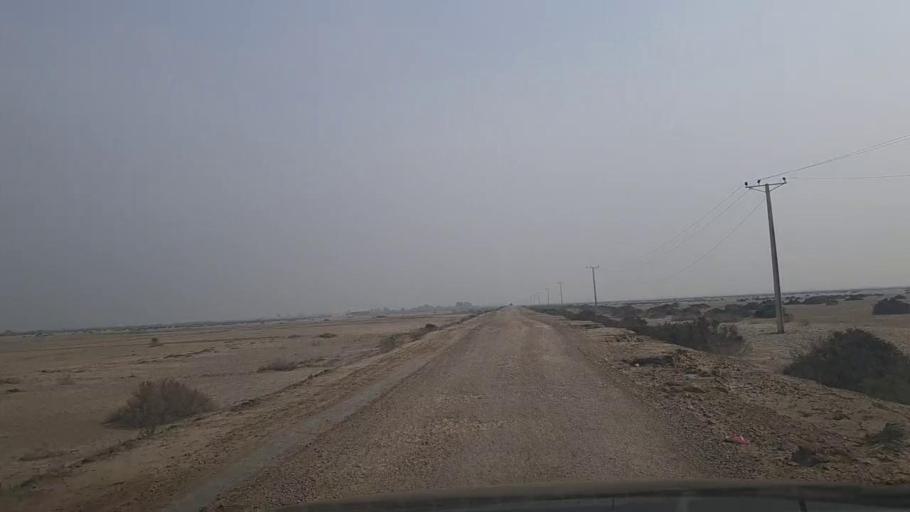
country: PK
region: Sindh
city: Mirpur Sakro
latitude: 24.4656
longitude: 67.6847
